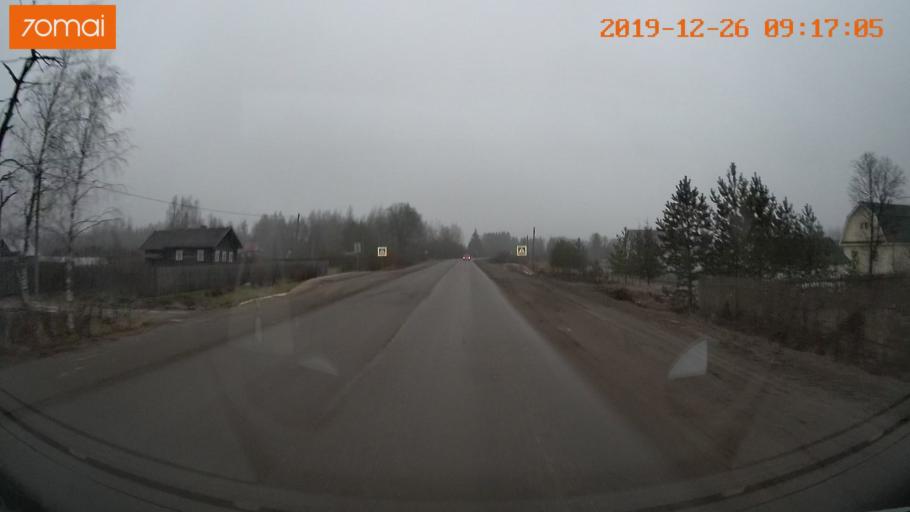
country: RU
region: Vologda
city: Gryazovets
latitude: 58.9258
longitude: 40.2389
